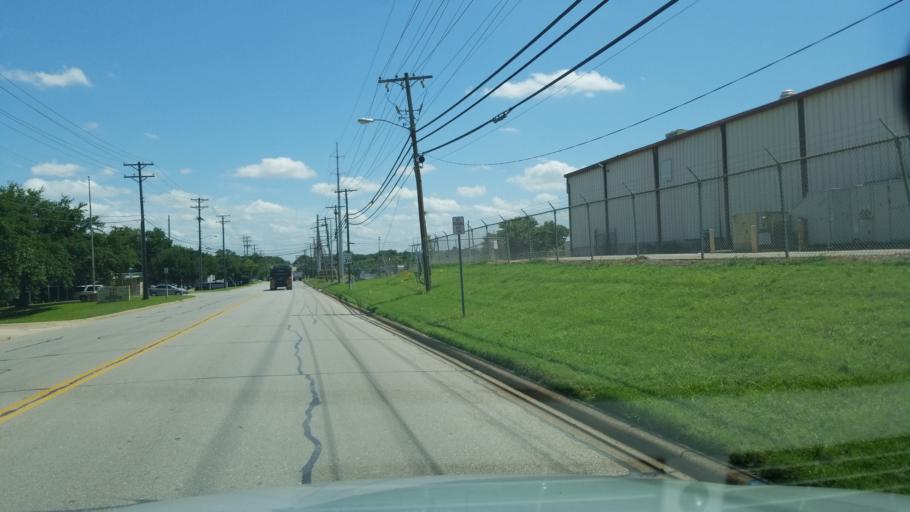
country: US
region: Texas
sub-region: Dallas County
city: Irving
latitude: 32.8196
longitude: -96.9170
